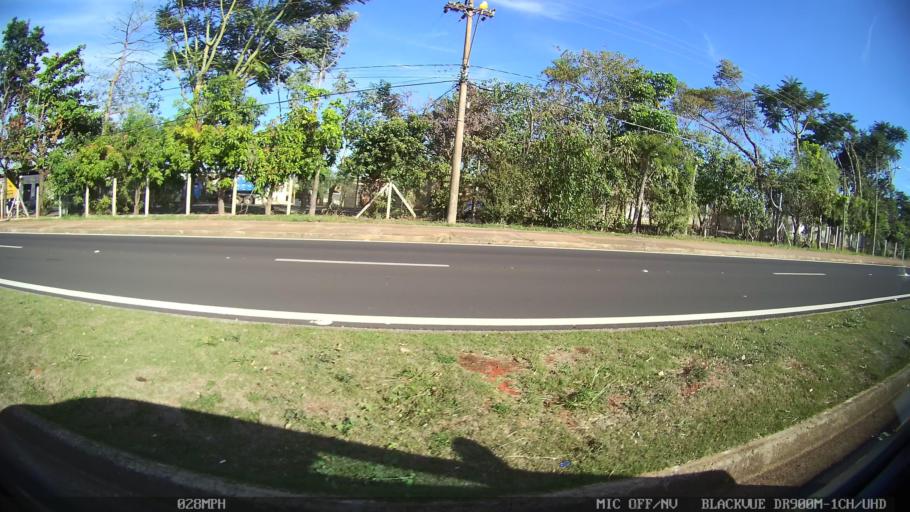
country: BR
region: Sao Paulo
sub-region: Araraquara
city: Araraquara
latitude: -21.7910
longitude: -48.1522
